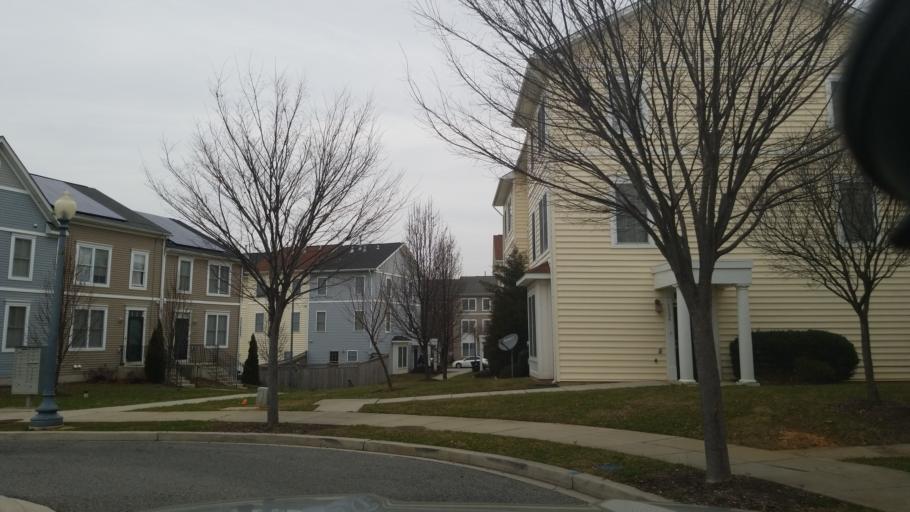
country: US
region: Maryland
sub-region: Prince George's County
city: Hillcrest Heights
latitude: 38.8476
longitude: -76.9816
